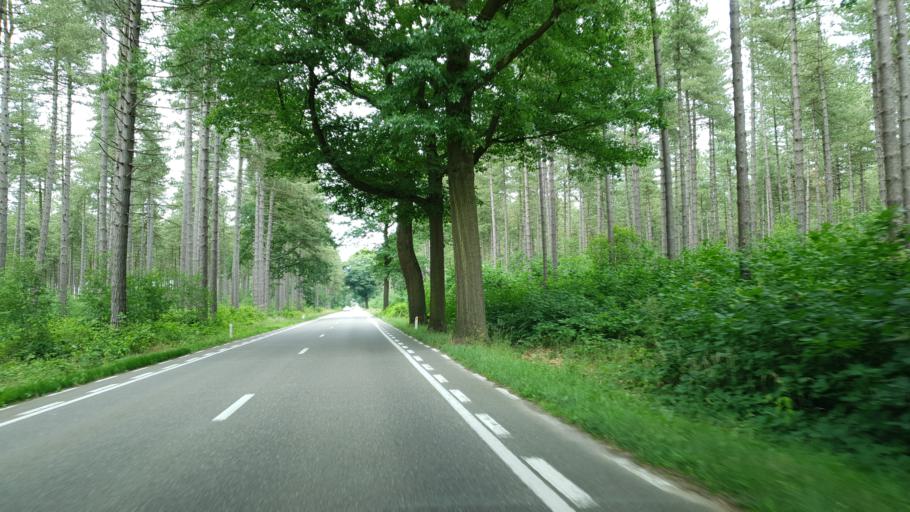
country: BE
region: Flanders
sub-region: Provincie Vlaams-Brabant
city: Scherpenheuvel-Zichem
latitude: 51.0440
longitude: 4.9864
